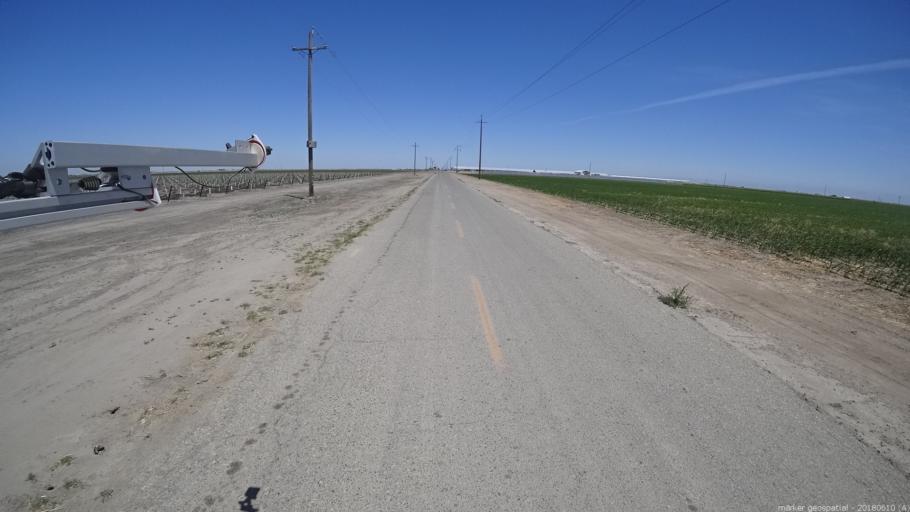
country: US
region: California
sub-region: Merced County
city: Dos Palos
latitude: 37.0522
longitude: -120.5287
